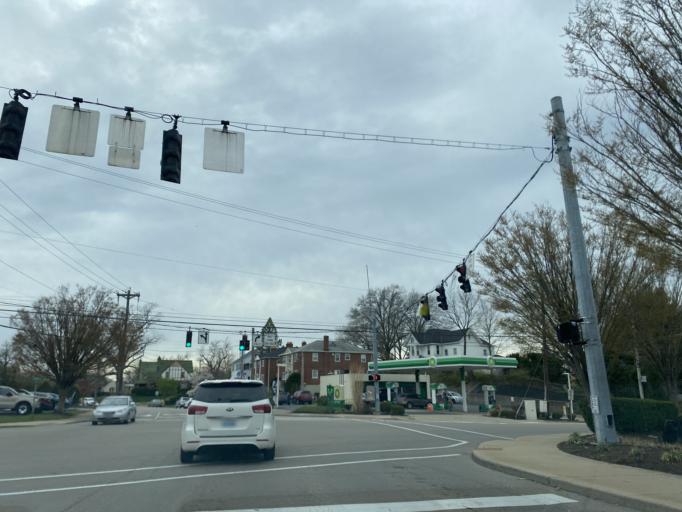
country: US
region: Kentucky
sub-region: Campbell County
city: Southgate
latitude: 39.0758
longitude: -84.4622
